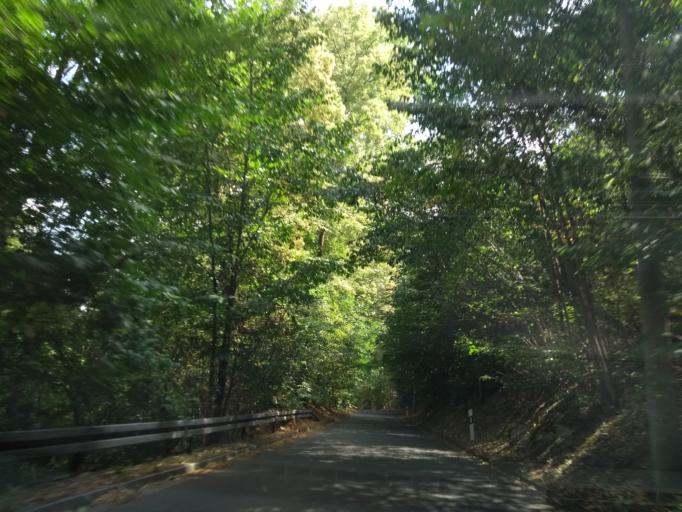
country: DE
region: Thuringia
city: Walpernhain
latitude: 51.0043
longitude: 11.9643
